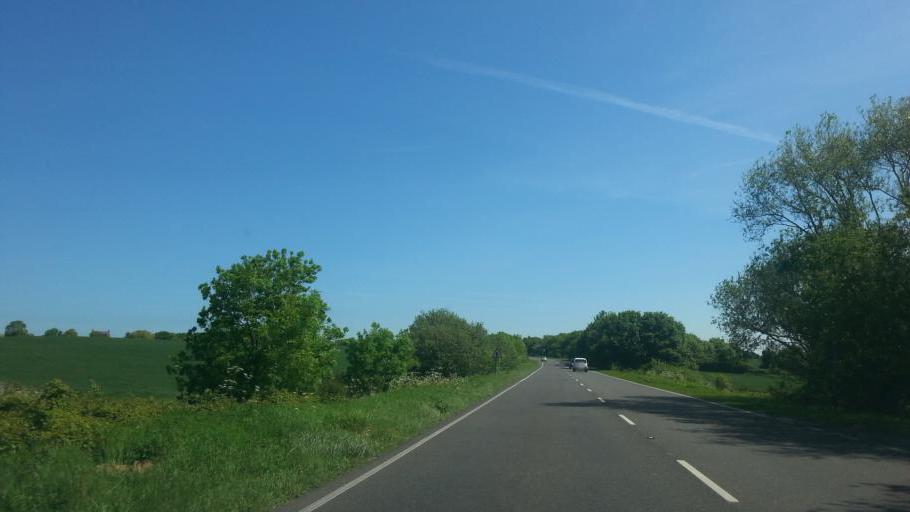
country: GB
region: England
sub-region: Cambridgeshire
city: Godmanchester
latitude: 52.3462
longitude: -0.1424
